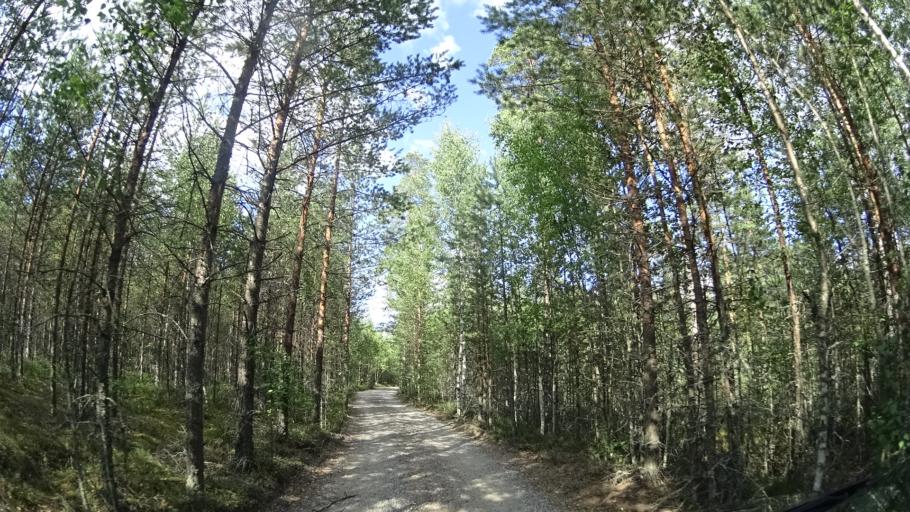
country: FI
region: Uusimaa
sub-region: Helsinki
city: Kaerkoelae
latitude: 60.7421
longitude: 24.0648
